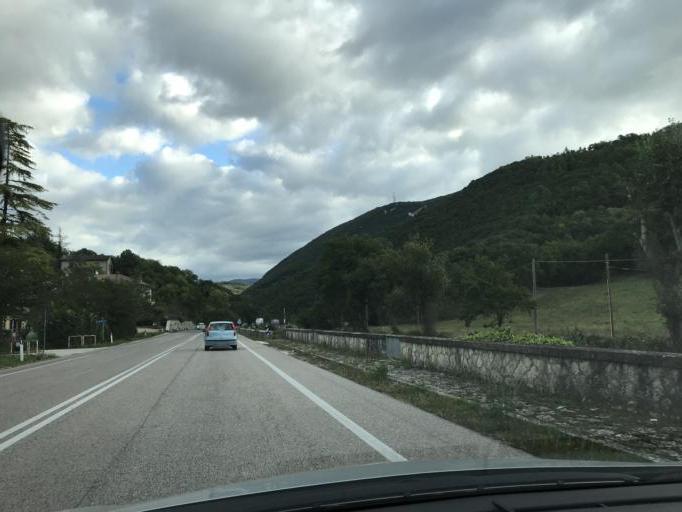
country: IT
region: Umbria
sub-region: Provincia di Perugia
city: Spoleto
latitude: 42.7208
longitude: 12.7302
